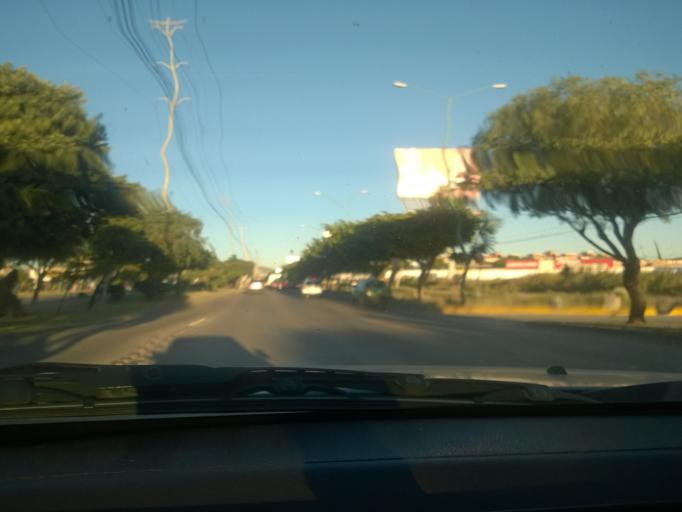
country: MX
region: Guanajuato
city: Leon
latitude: 21.1475
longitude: -101.6541
